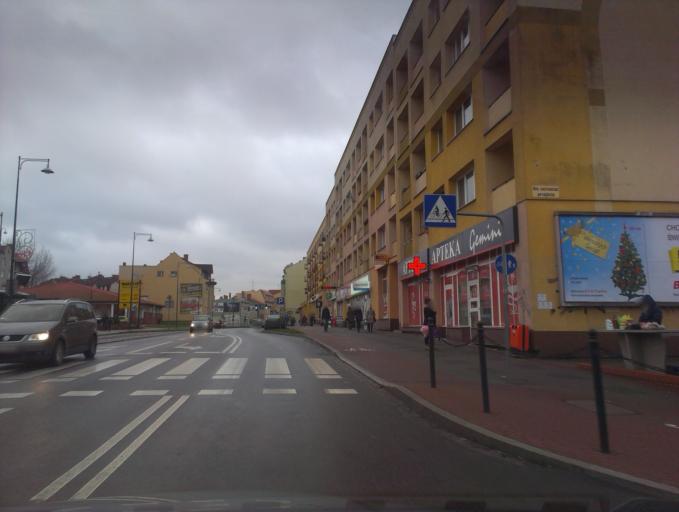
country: PL
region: West Pomeranian Voivodeship
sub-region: Powiat szczecinecki
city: Szczecinek
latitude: 53.7070
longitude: 16.6986
